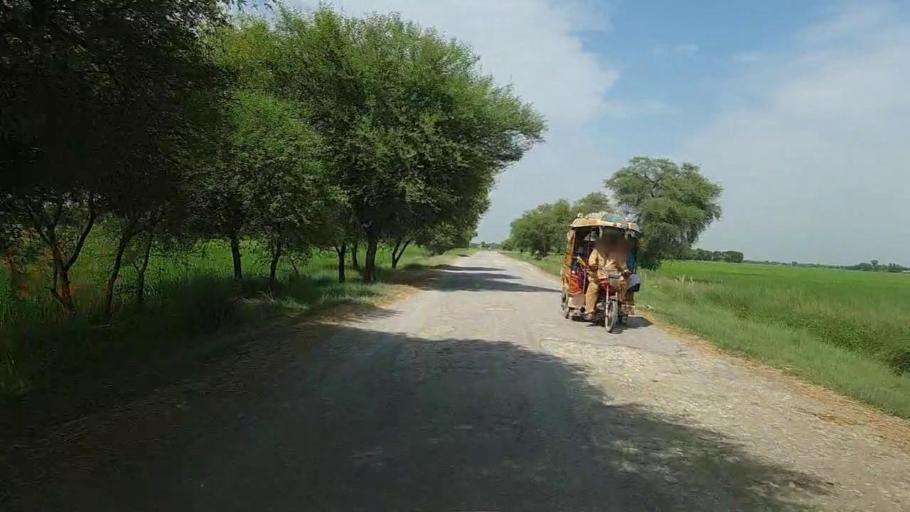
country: PK
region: Sindh
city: Thul
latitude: 28.2338
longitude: 68.7974
